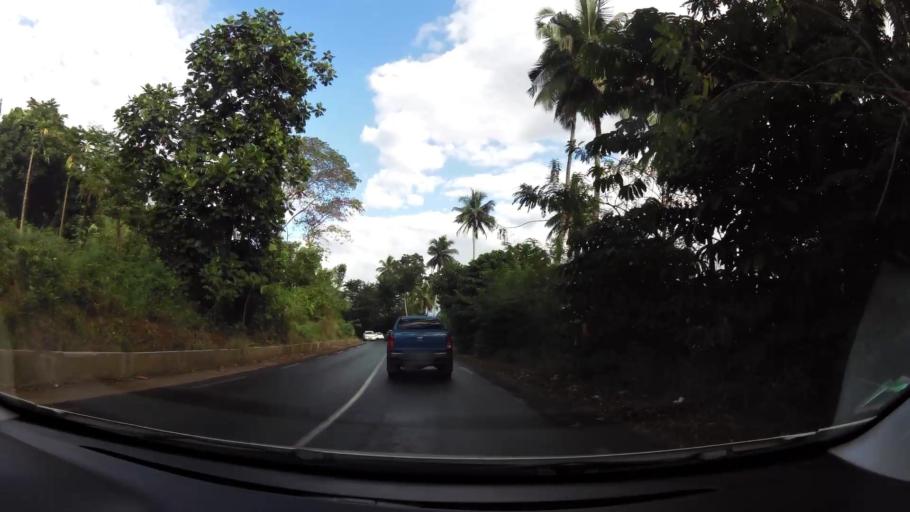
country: YT
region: Ouangani
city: Ouangani
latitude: -12.8358
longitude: 45.1481
